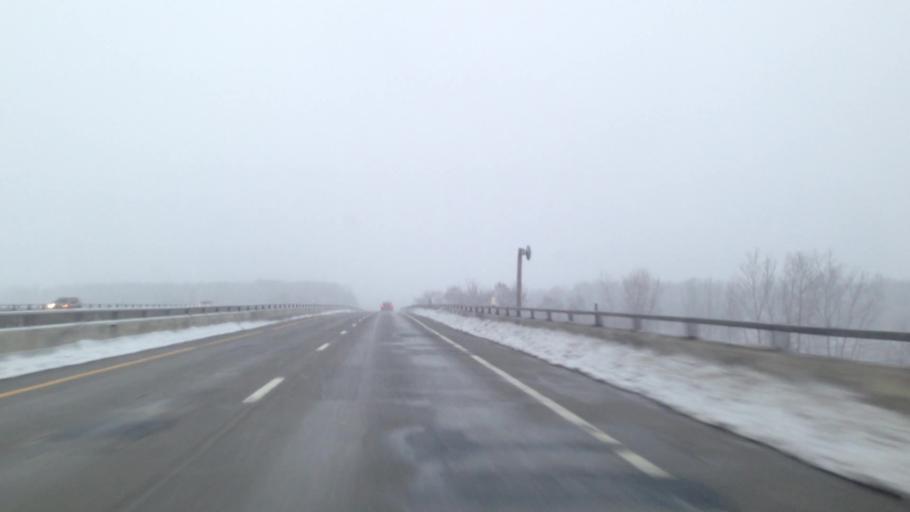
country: US
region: New York
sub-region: Onondaga County
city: East Syracuse
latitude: 43.0670
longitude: -76.0525
